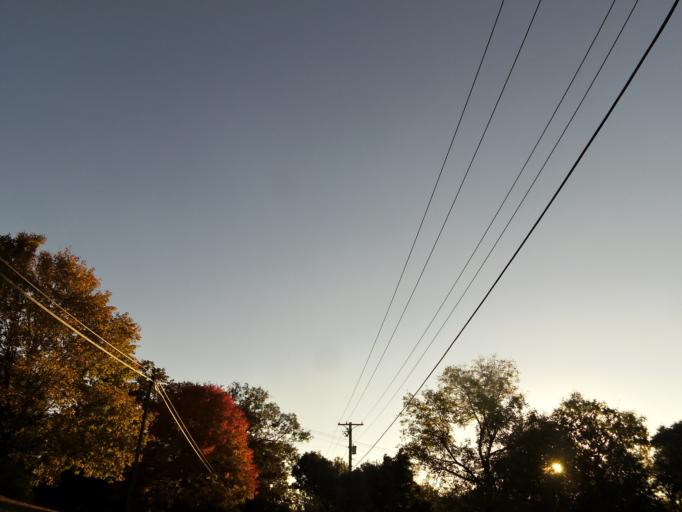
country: US
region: Tennessee
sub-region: Anderson County
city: Clinton
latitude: 36.0128
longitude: -84.0534
